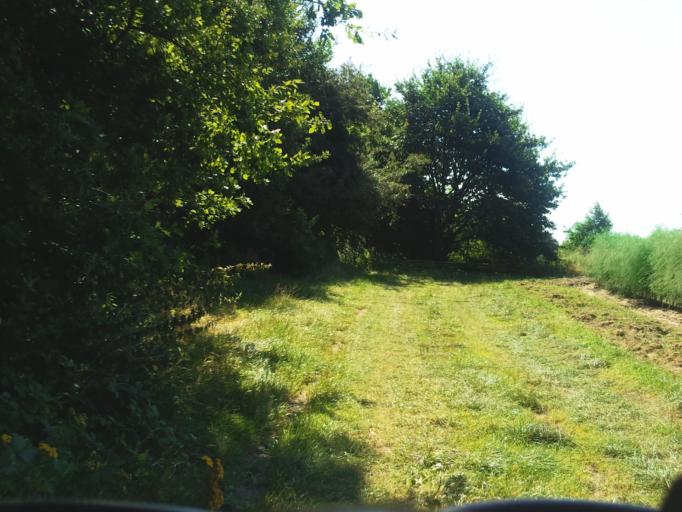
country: DE
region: Lower Saxony
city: Nienburg
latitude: 52.6513
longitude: 9.2375
